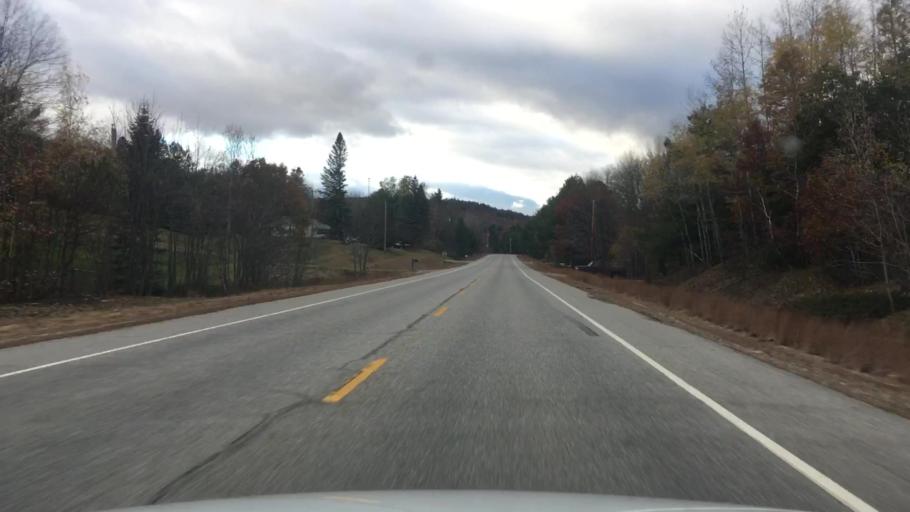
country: US
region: Maine
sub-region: Oxford County
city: Canton
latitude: 44.4183
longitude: -70.2888
